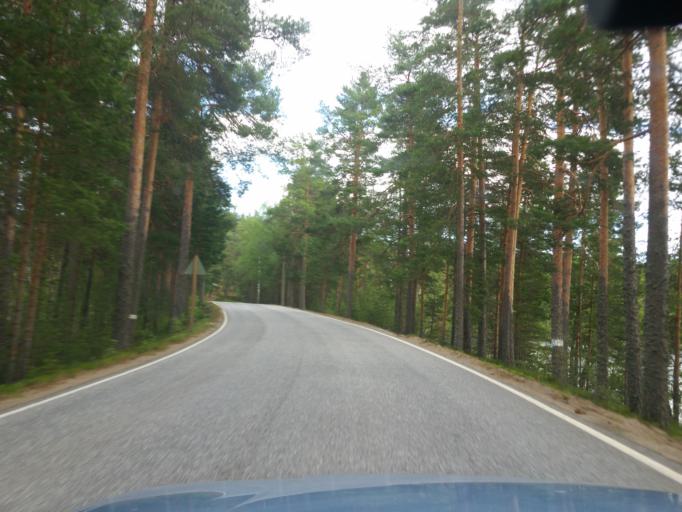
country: FI
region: Southern Savonia
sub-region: Savonlinna
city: Sulkava
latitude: 61.7741
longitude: 28.4297
